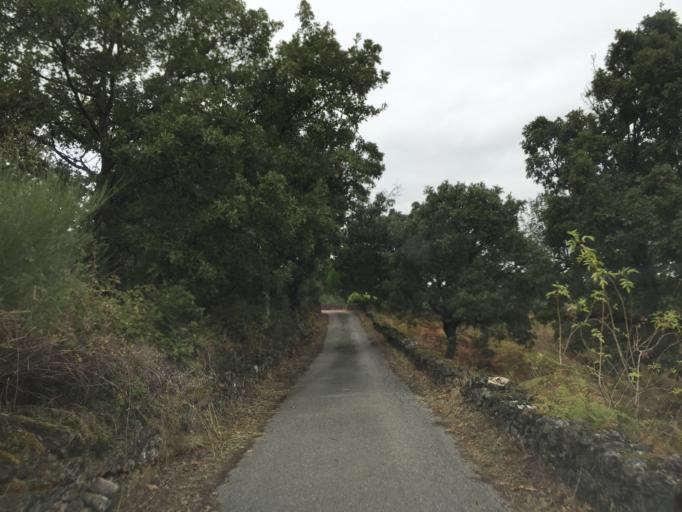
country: PT
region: Portalegre
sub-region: Marvao
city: Marvao
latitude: 39.4032
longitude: -7.3723
